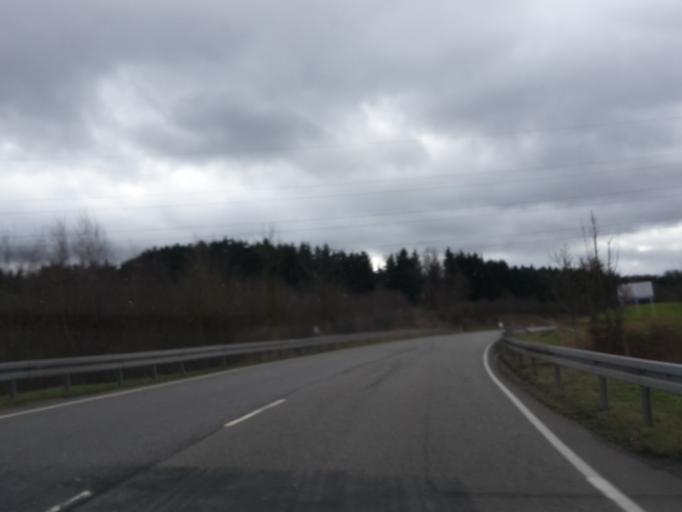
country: DE
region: Hesse
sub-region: Regierungsbezirk Darmstadt
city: Idstein
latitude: 50.1704
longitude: 8.2219
